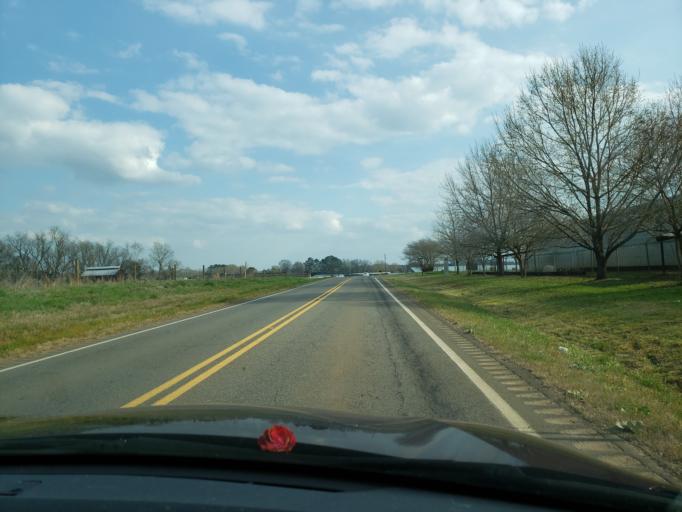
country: US
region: Alabama
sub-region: Hale County
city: Greensboro
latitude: 32.7187
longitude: -87.6207
